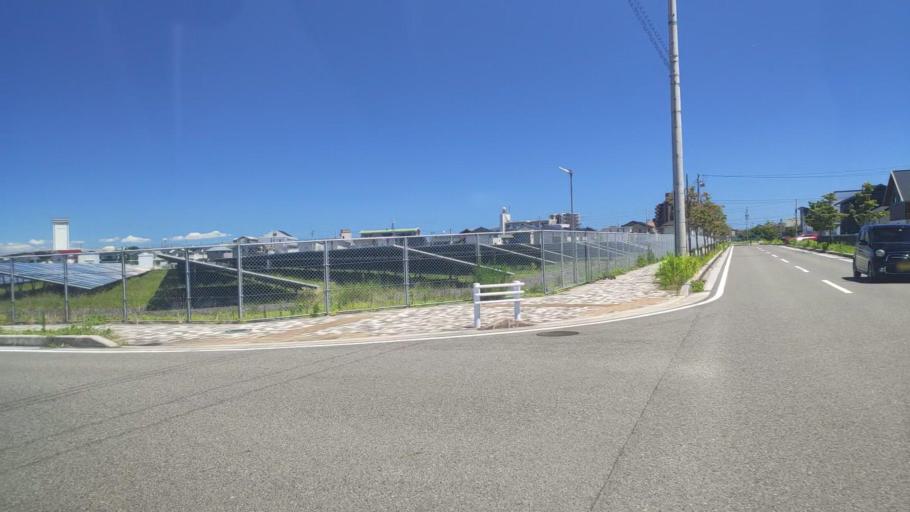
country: JP
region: Mie
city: Suzuka
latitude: 34.8484
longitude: 136.5847
